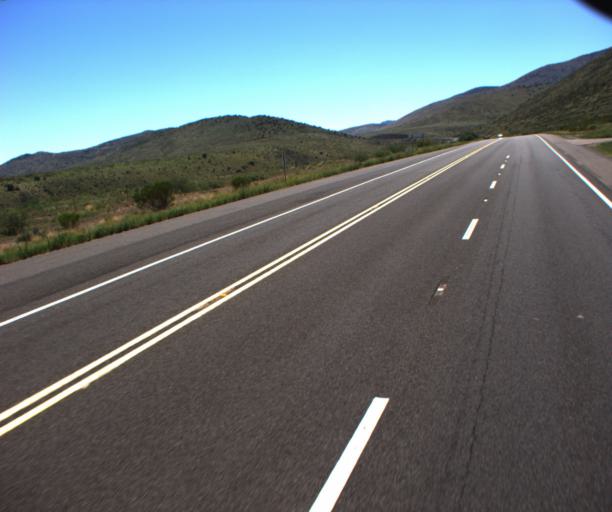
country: US
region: Arizona
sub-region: Greenlee County
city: Clifton
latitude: 32.9074
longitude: -109.2594
